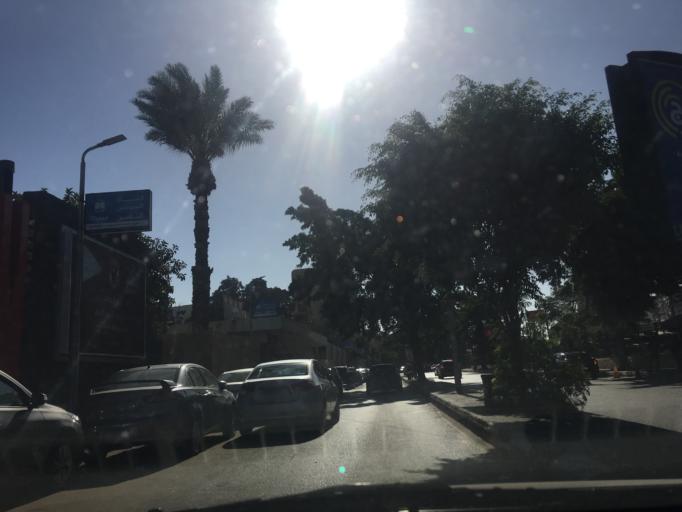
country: EG
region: Muhafazat al Qahirah
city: Cairo
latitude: 30.0452
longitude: 31.2205
